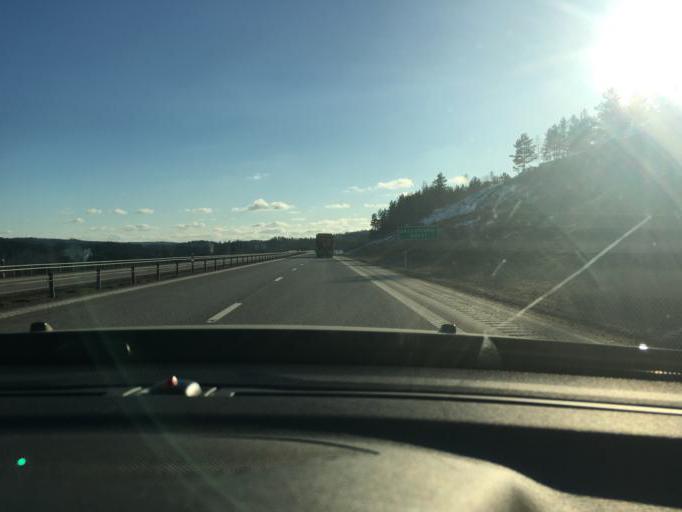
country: SE
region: Vaestra Goetaland
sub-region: Boras Kommun
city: Dalsjofors
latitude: 57.7698
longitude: 13.1132
